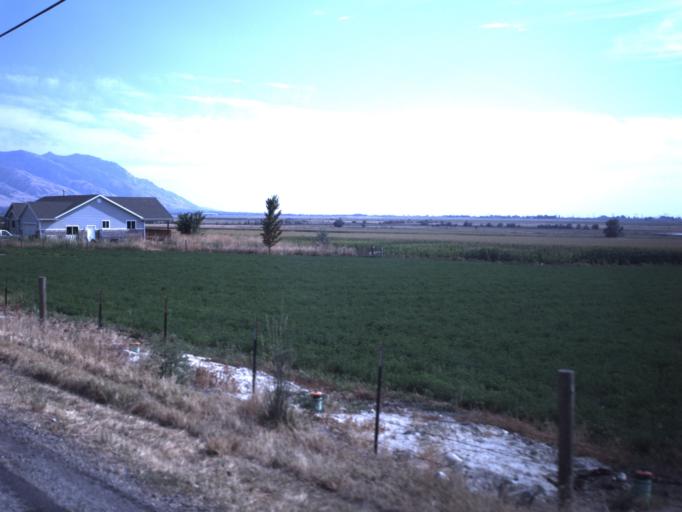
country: US
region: Utah
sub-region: Box Elder County
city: Honeyville
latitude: 41.6055
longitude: -112.0578
